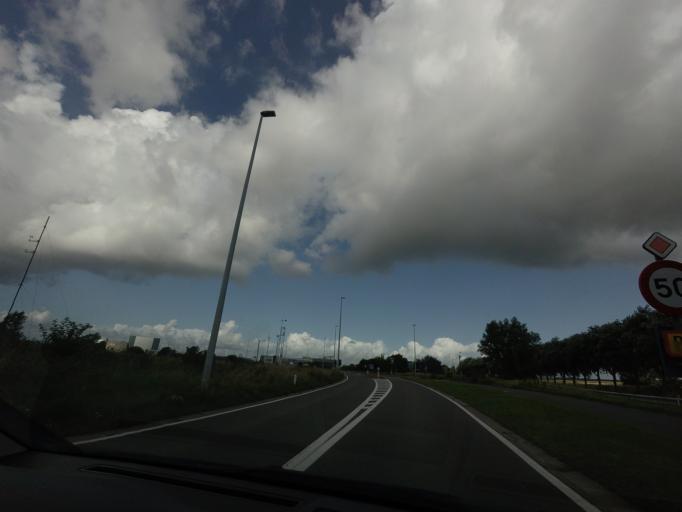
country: BE
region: Flanders
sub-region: Provincie West-Vlaanderen
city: Oudenburg
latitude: 51.2145
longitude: 2.9984
